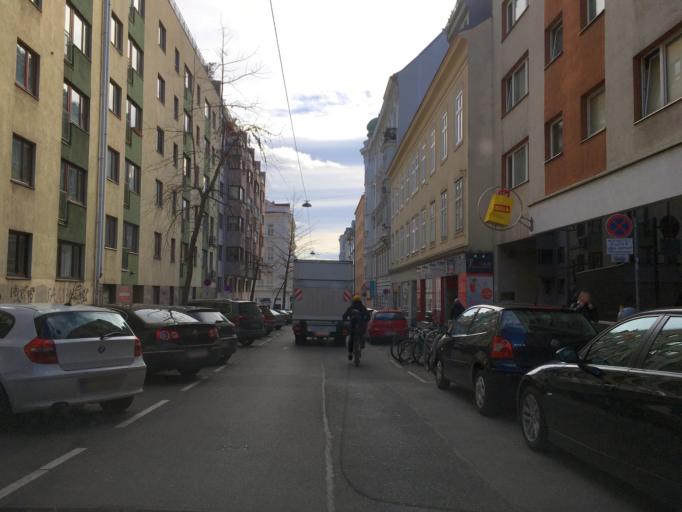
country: AT
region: Vienna
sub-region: Wien Stadt
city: Vienna
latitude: 48.1956
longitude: 16.3451
